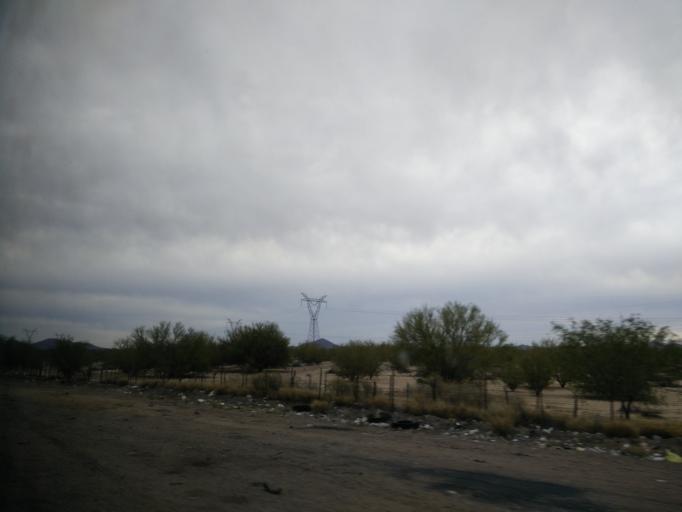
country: MX
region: Sonora
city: Hermosillo
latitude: 28.6872
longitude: -110.9906
